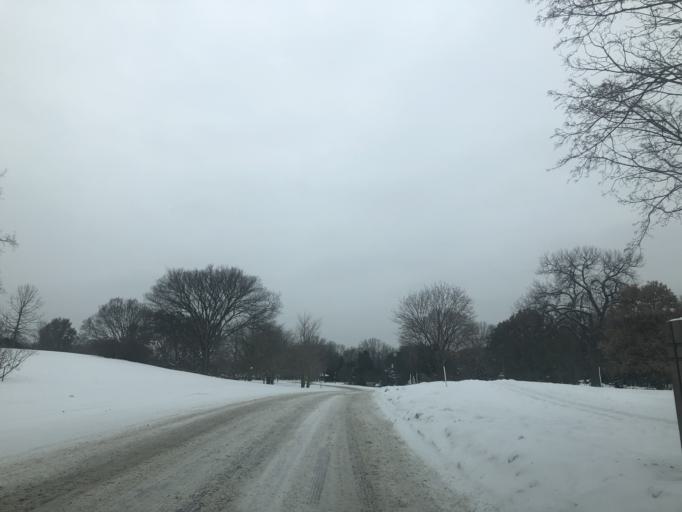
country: US
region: Minnesota
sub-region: Hennepin County
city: Richfield
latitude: 44.9292
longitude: -93.2941
